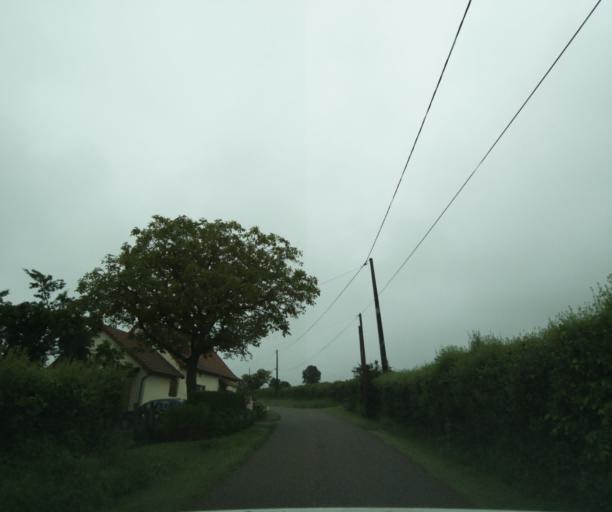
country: FR
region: Bourgogne
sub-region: Departement de Saone-et-Loire
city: Charolles
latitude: 46.4301
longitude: 4.4161
